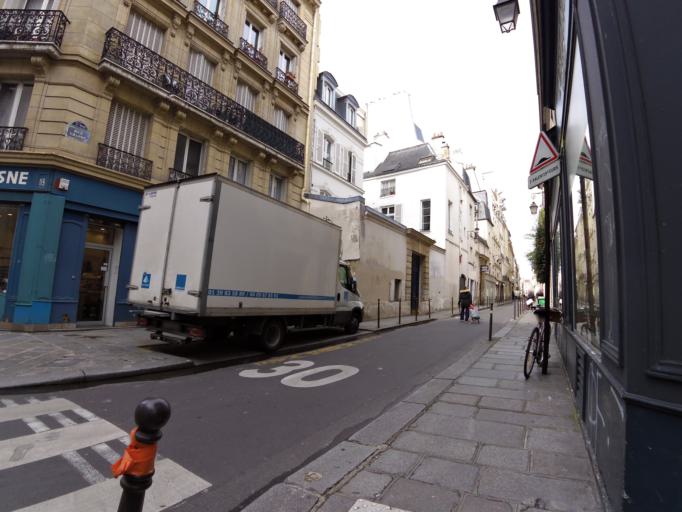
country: FR
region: Ile-de-France
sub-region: Paris
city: Paris
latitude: 48.8628
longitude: 2.3579
